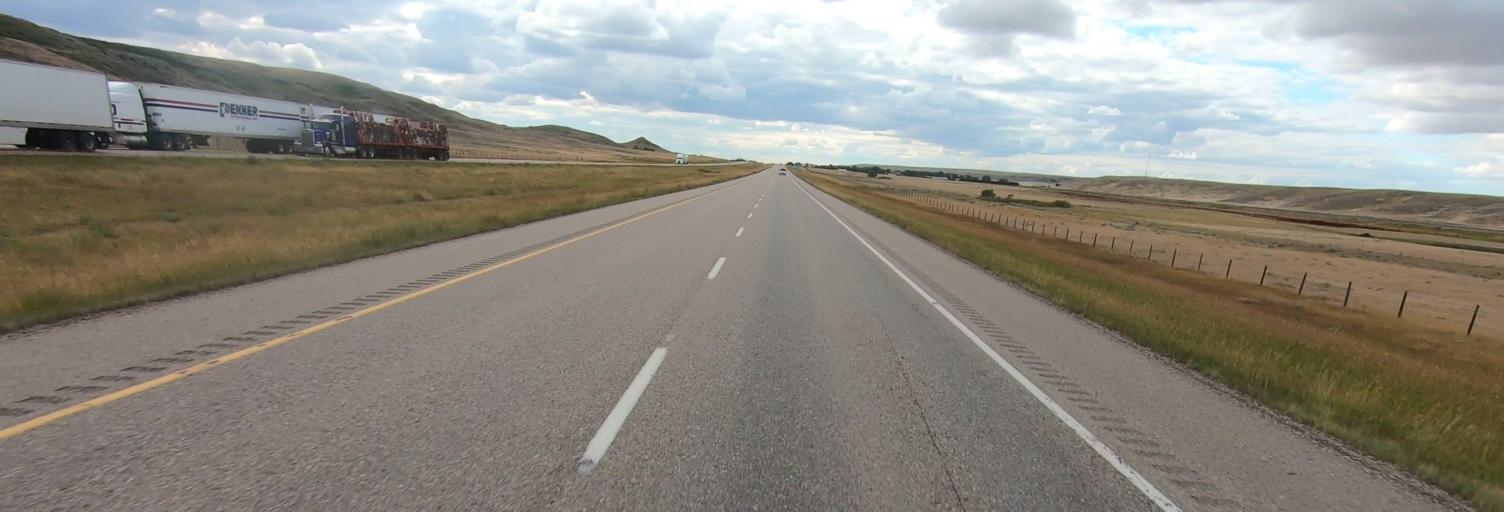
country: CA
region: Alberta
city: Medicine Hat
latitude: 49.9520
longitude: -110.2442
